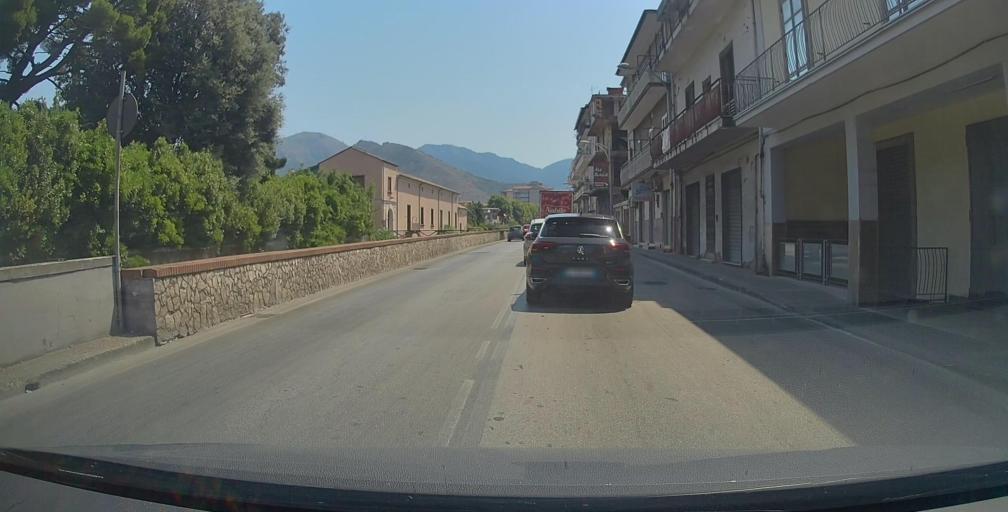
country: IT
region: Campania
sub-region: Provincia di Salerno
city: Nocera Superiore
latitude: 40.7404
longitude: 14.6651
